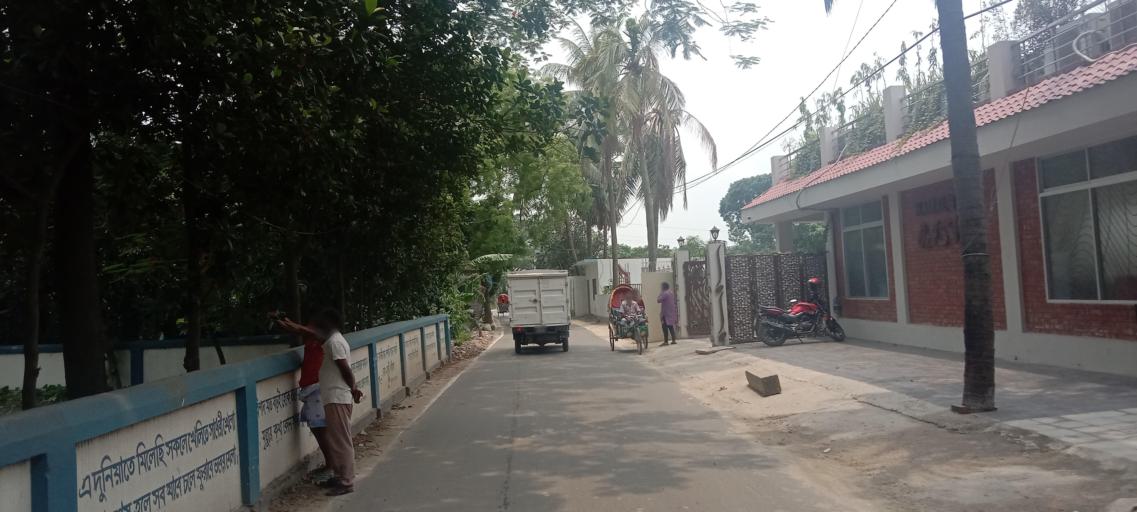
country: BD
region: Dhaka
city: Azimpur
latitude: 23.7188
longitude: 90.3450
